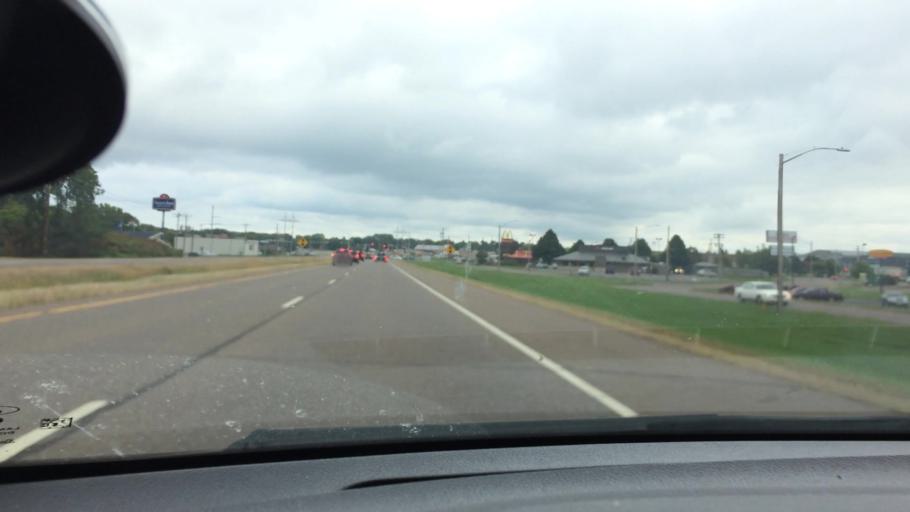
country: US
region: Wisconsin
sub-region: Chippewa County
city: Chippewa Falls
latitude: 44.9136
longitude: -91.3933
